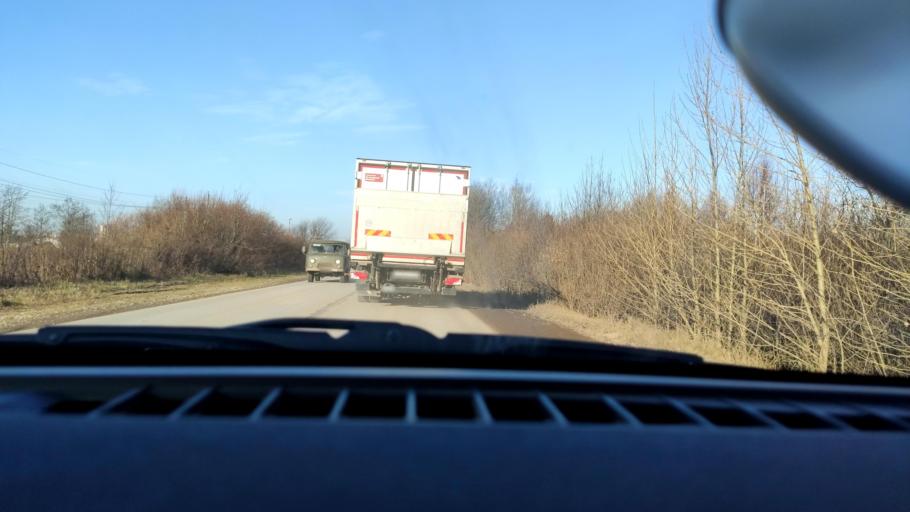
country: RU
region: Perm
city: Kondratovo
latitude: 58.0053
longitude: 56.0577
